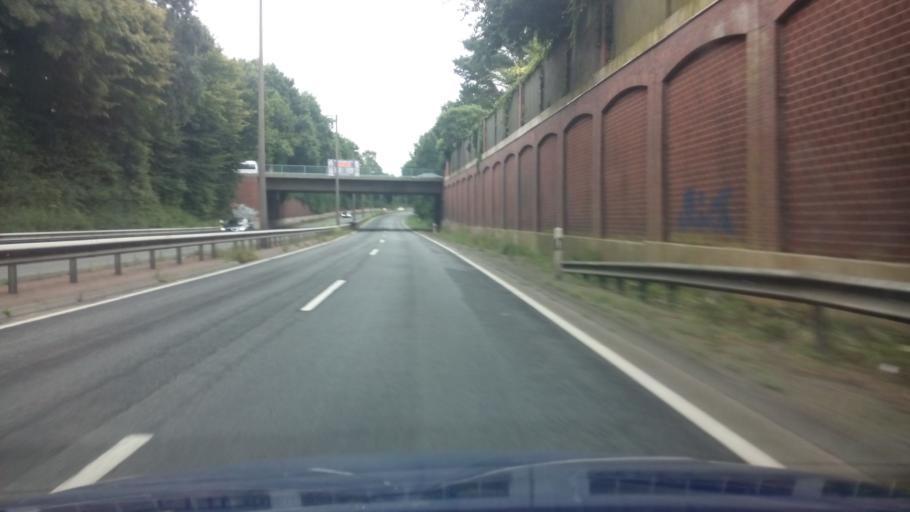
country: DE
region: Lower Saxony
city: Lemwerder
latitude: 53.1810
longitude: 8.5972
